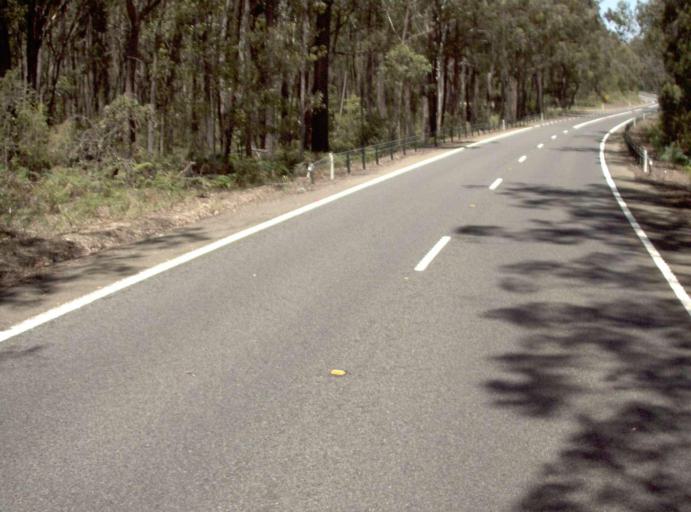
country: AU
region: Victoria
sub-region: East Gippsland
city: Lakes Entrance
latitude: -37.7892
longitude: 148.0526
